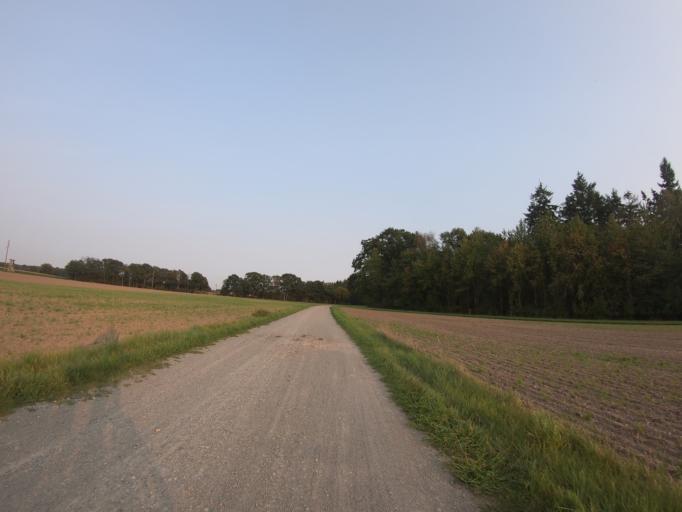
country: DE
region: Lower Saxony
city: Leiferde
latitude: 52.4295
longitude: 10.4656
